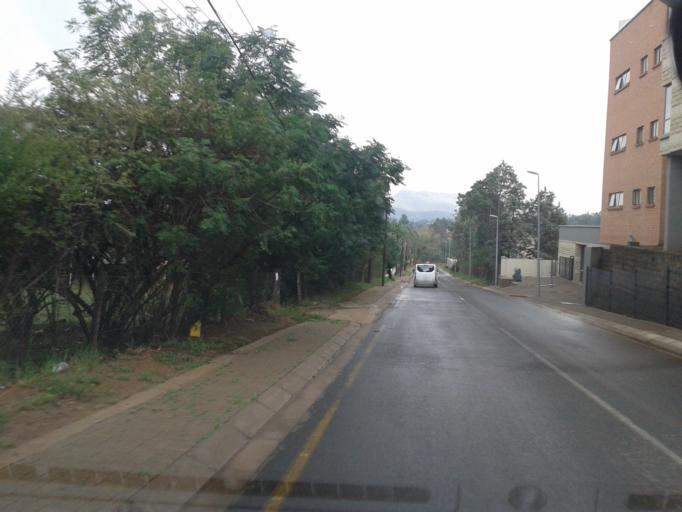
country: LS
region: Maseru
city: Maseru
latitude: -29.3138
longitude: 27.4726
